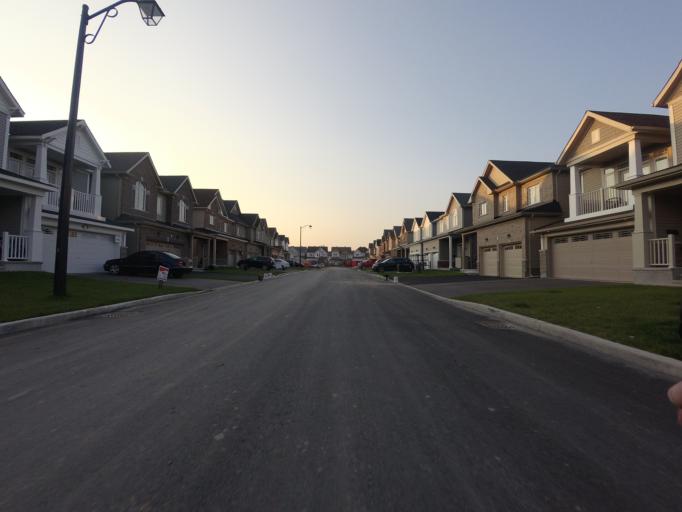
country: CA
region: Ontario
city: Bells Corners
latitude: 45.2768
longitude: -75.8436
